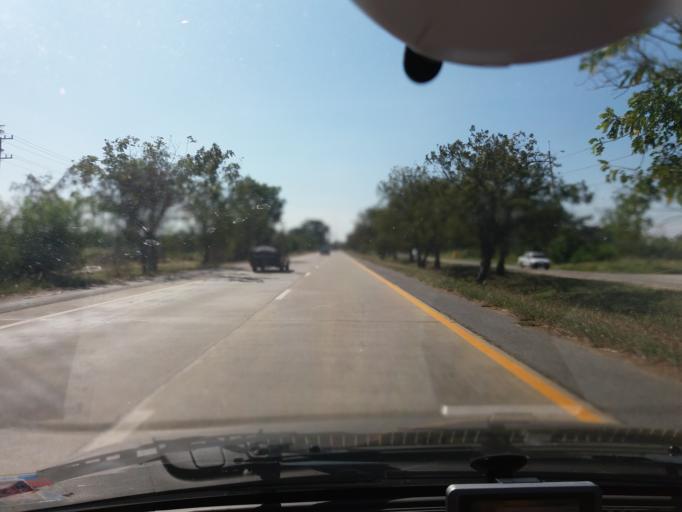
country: TH
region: Suphan Buri
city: Doembang Nangbuat
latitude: 14.8206
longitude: 100.1157
